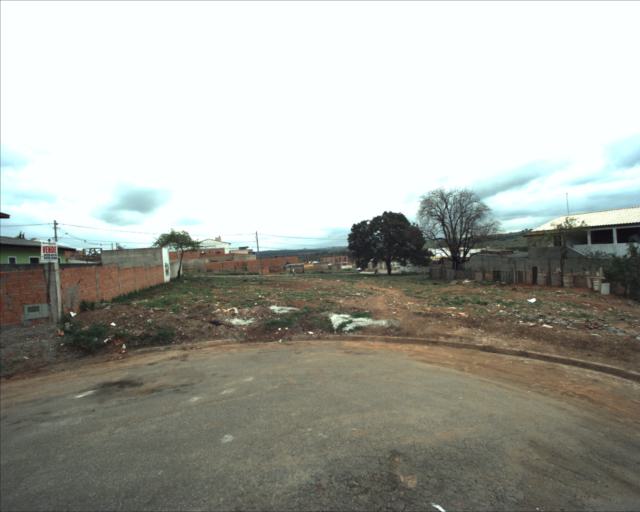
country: BR
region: Sao Paulo
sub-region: Sorocaba
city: Sorocaba
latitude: -23.4312
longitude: -47.5010
